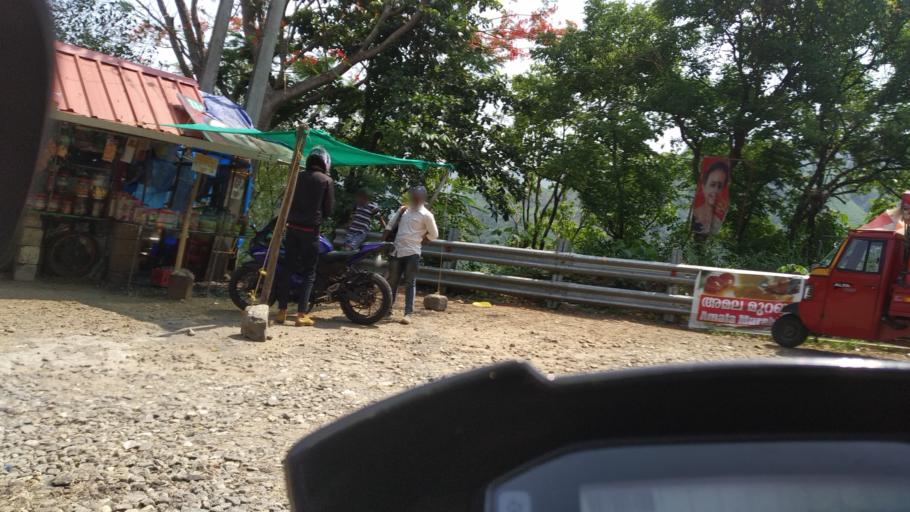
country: IN
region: Kerala
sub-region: Kottayam
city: Erattupetta
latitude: 9.7012
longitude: 76.8646
